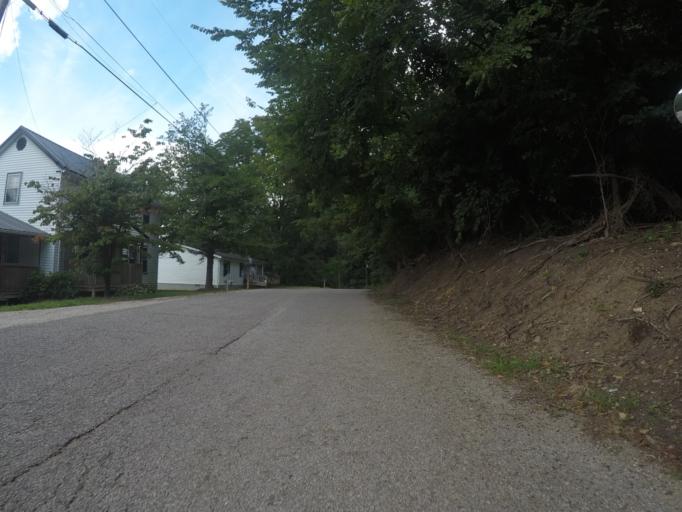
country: US
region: West Virginia
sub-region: Cabell County
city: Pea Ridge
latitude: 38.4224
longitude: -82.3800
